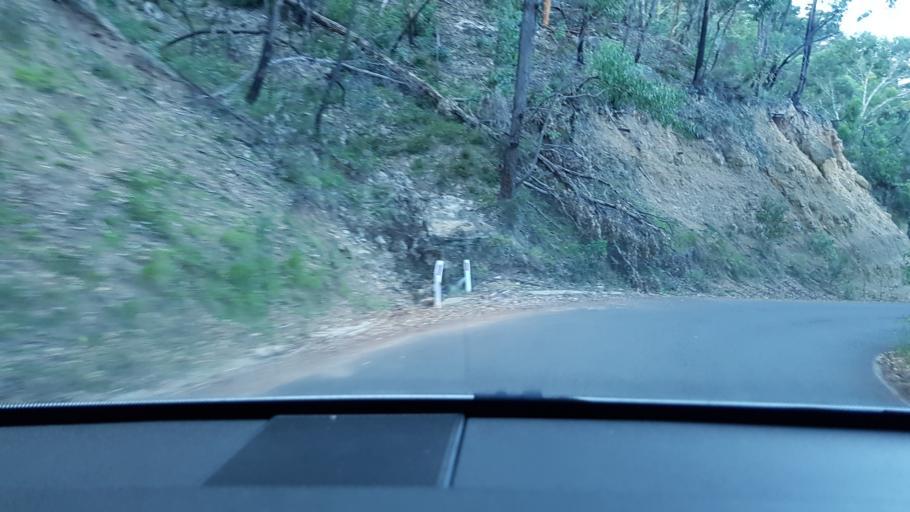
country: AU
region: New South Wales
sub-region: Lithgow
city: Portland
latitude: -33.3065
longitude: 150.1150
